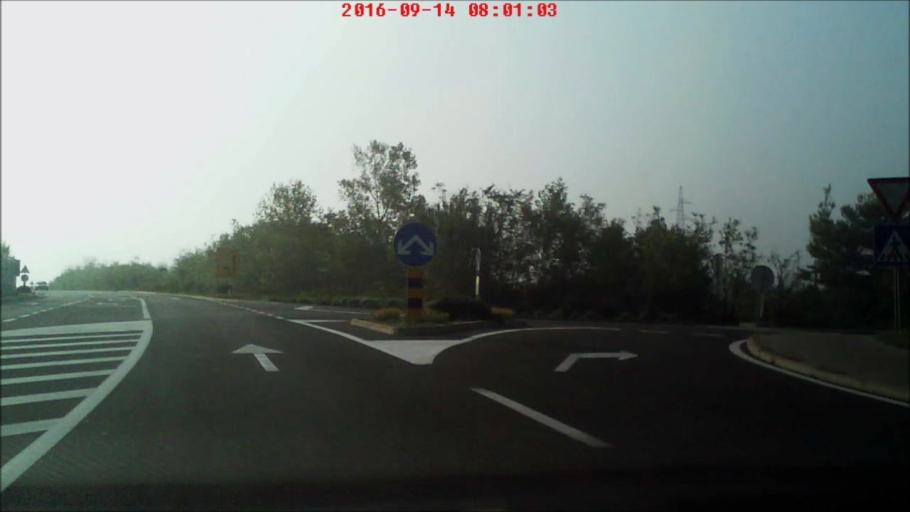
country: HR
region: Zadarska
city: Nin
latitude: 44.2542
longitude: 15.1573
